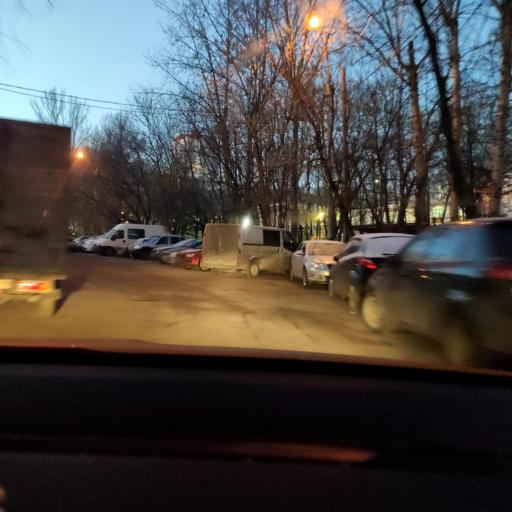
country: RU
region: Moscow
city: Veshnyaki
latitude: 55.7167
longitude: 37.8245
